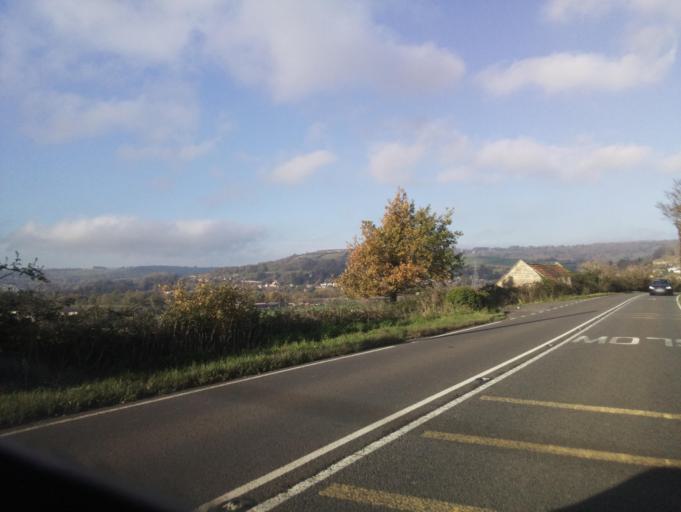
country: GB
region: England
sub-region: Bath and North East Somerset
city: Freshford
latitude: 51.3972
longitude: -2.3072
